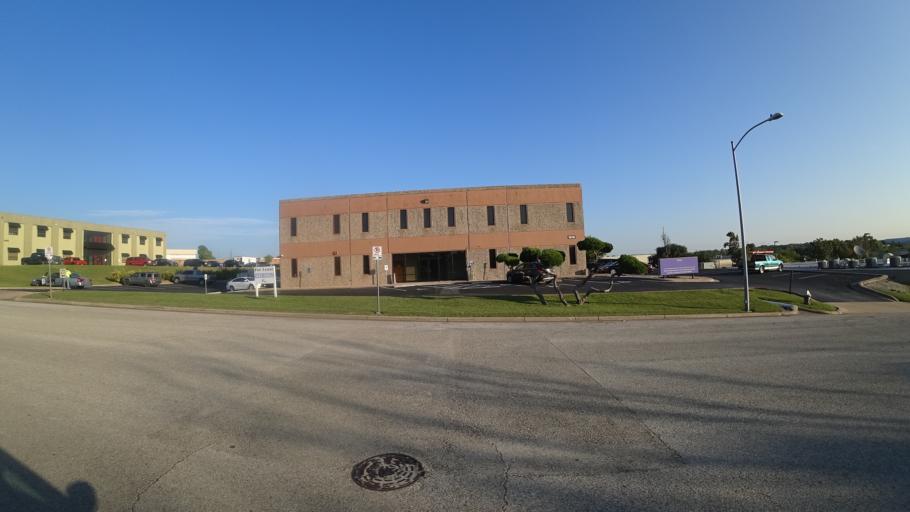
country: US
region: Texas
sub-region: Travis County
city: Austin
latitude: 30.3340
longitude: -97.6821
